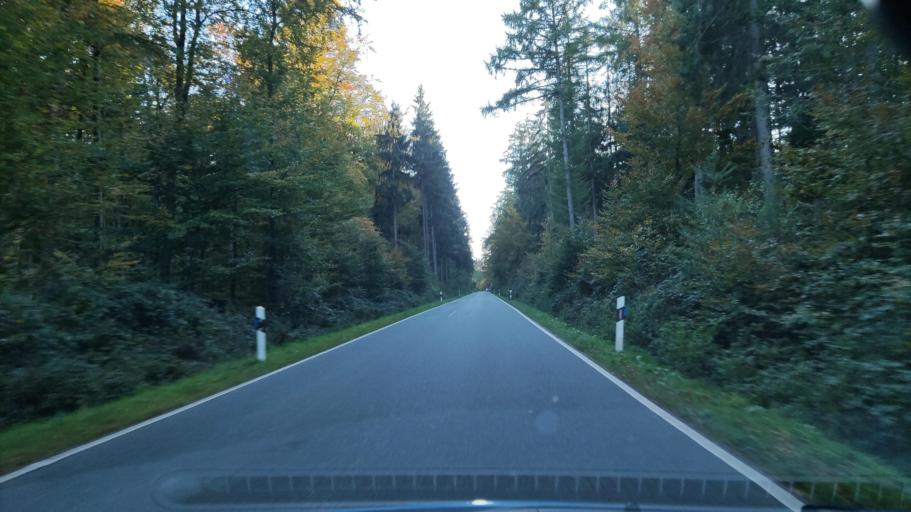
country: DE
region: Schleswig-Holstein
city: Schwarzenbek
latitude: 53.5178
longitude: 10.4579
